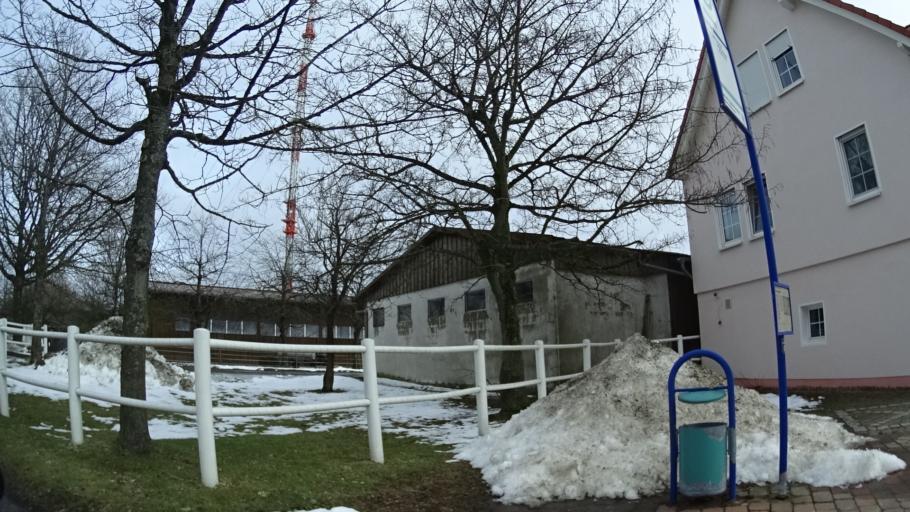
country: DE
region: Hesse
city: Michelstadt
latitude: 49.6569
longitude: 9.0675
